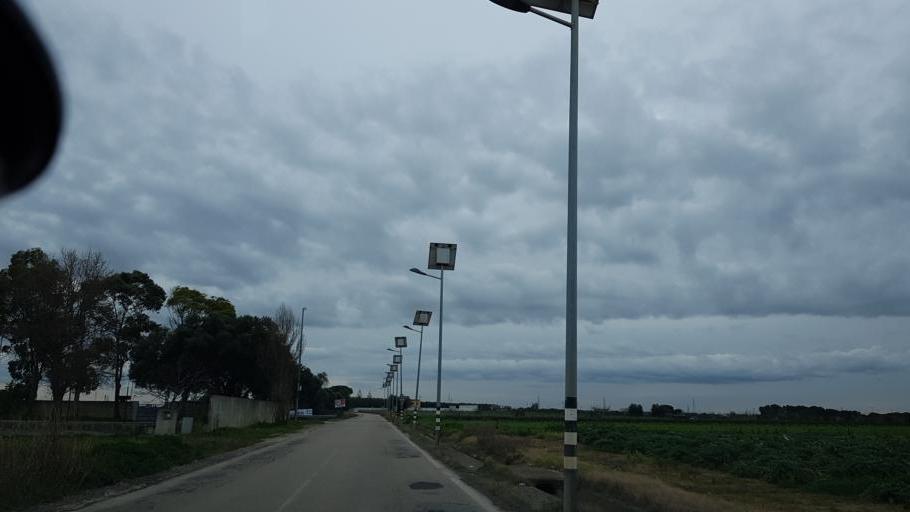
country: IT
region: Apulia
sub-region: Provincia di Brindisi
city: La Rosa
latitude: 40.6150
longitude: 17.9449
